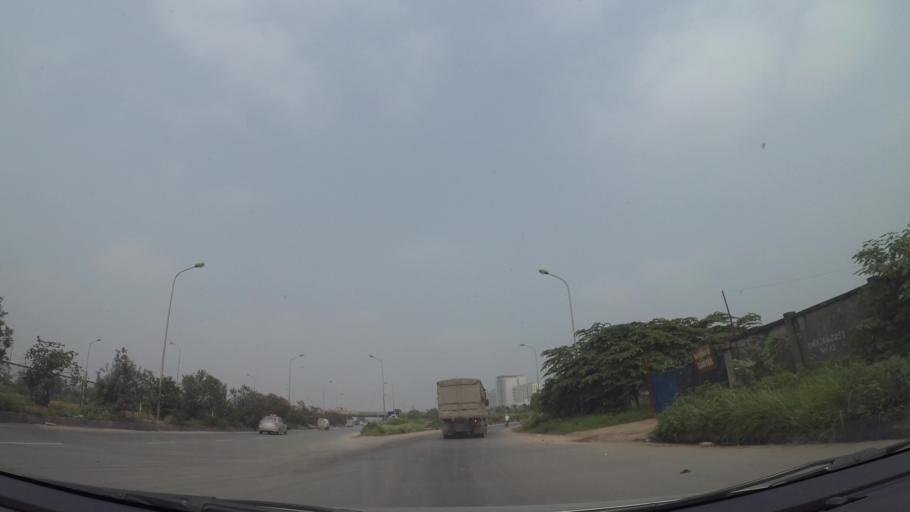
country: VN
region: Ha Noi
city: Cau Dien
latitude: 21.0096
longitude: 105.7499
